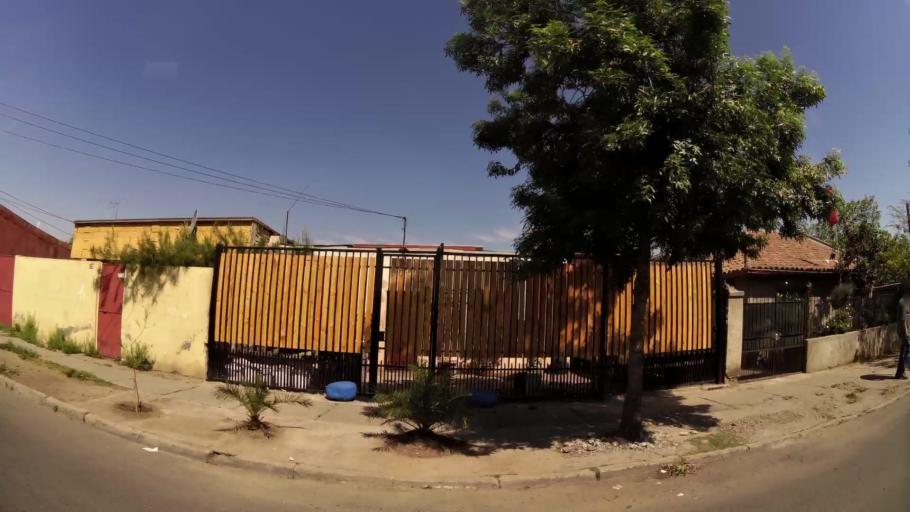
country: CL
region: Santiago Metropolitan
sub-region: Provincia de Santiago
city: La Pintana
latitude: -33.5347
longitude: -70.6419
